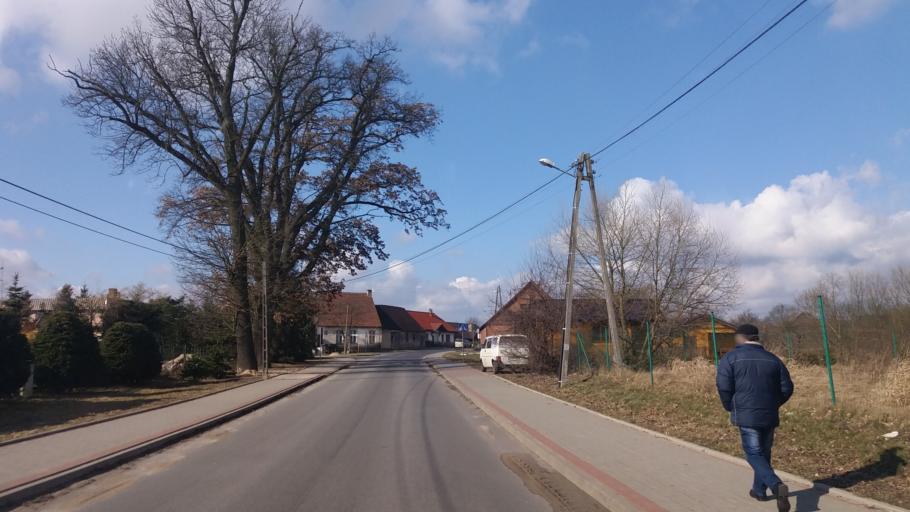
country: PL
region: West Pomeranian Voivodeship
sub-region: Powiat choszczenski
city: Drawno
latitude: 53.2216
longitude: 15.7560
